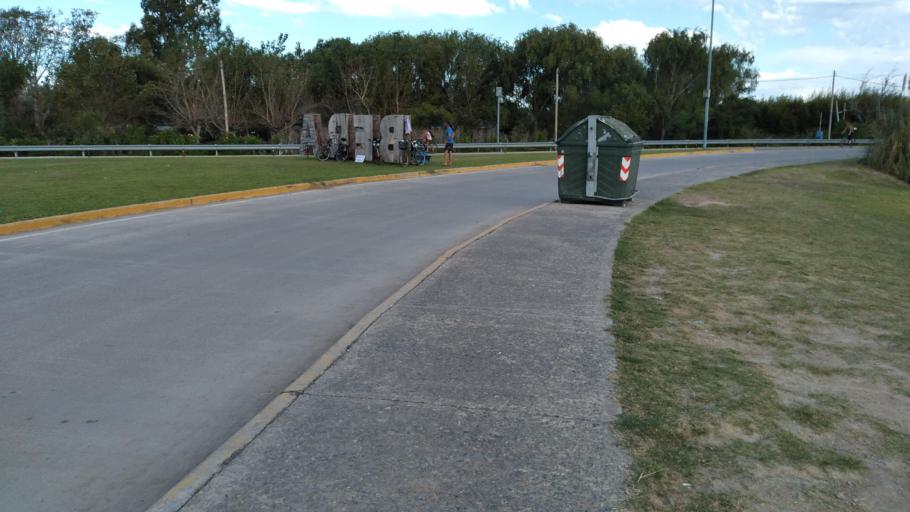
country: AR
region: Buenos Aires
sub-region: Partido de Quilmes
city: Quilmes
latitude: -34.7543
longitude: -58.1091
